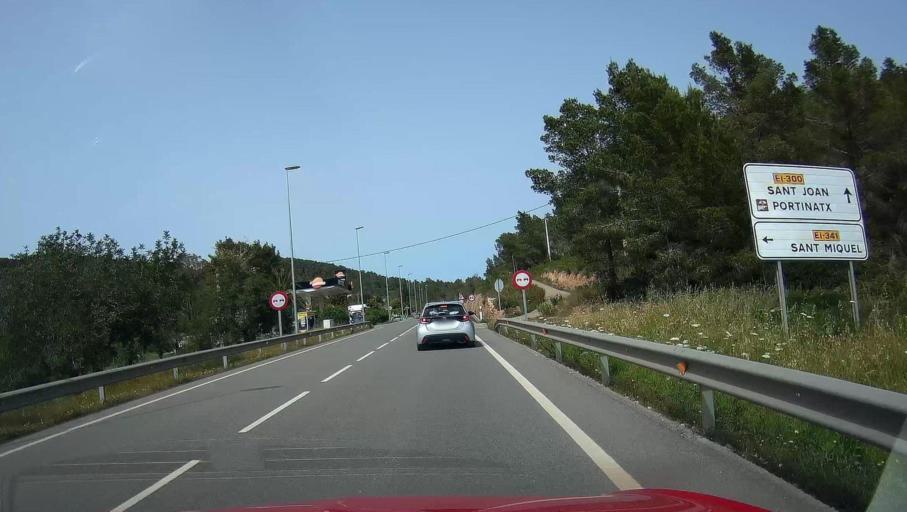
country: ES
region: Balearic Islands
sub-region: Illes Balears
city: Sant Joan de Labritja
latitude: 39.0695
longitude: 1.4959
